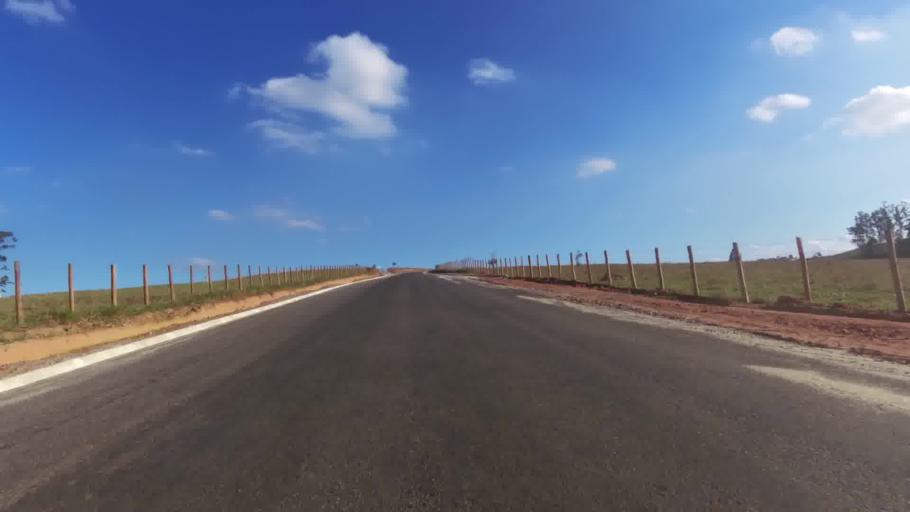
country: BR
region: Espirito Santo
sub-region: Marataizes
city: Marataizes
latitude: -21.1390
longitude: -41.0586
